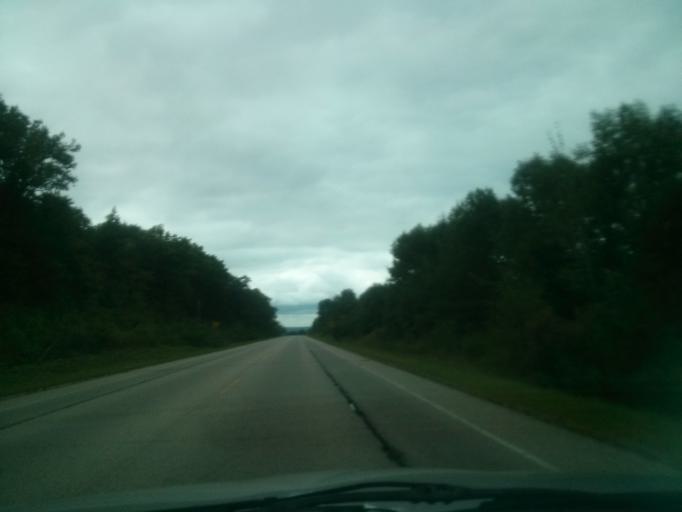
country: US
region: Wisconsin
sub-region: Pierce County
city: Spring Valley
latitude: 44.8320
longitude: -92.3342
